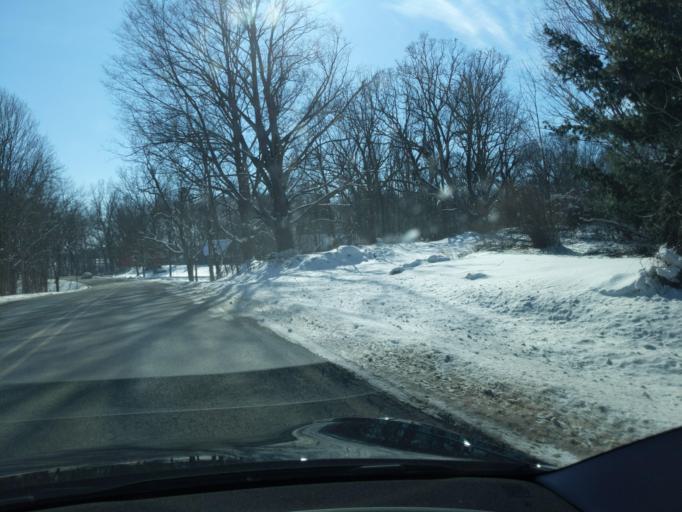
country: US
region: Michigan
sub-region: Livingston County
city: Fowlerville
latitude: 42.5546
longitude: -84.0718
